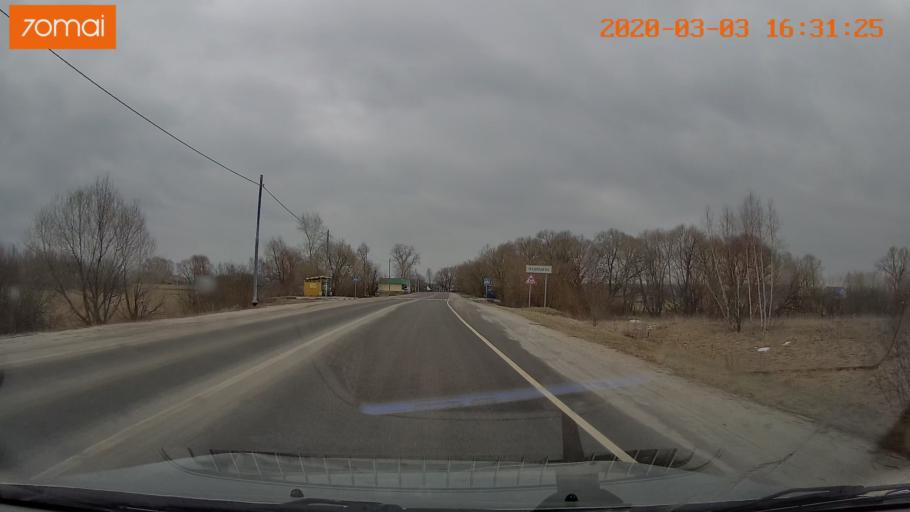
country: RU
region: Moskovskaya
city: Konobeyevo
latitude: 55.4253
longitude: 38.7247
